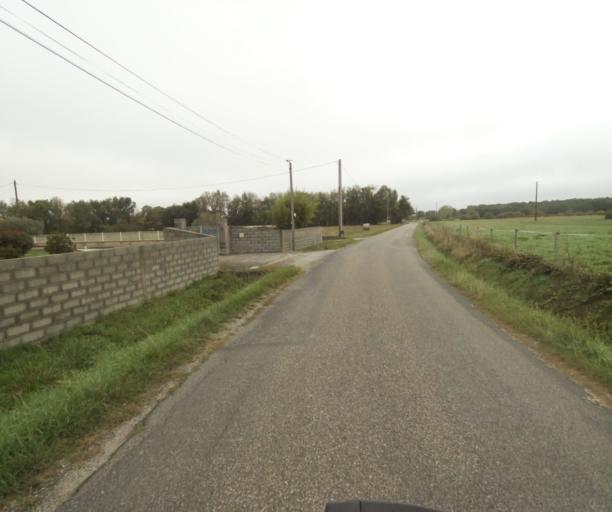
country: FR
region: Midi-Pyrenees
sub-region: Departement du Tarn-et-Garonne
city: Labastide-Saint-Pierre
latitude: 43.8875
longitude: 1.3807
